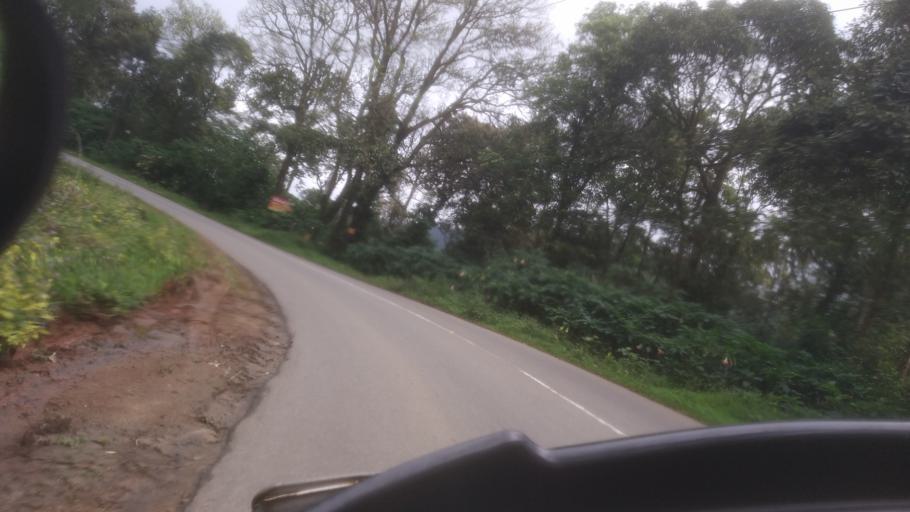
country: IN
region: Tamil Nadu
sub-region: Theni
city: Kombai
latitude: 9.8930
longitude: 77.1700
